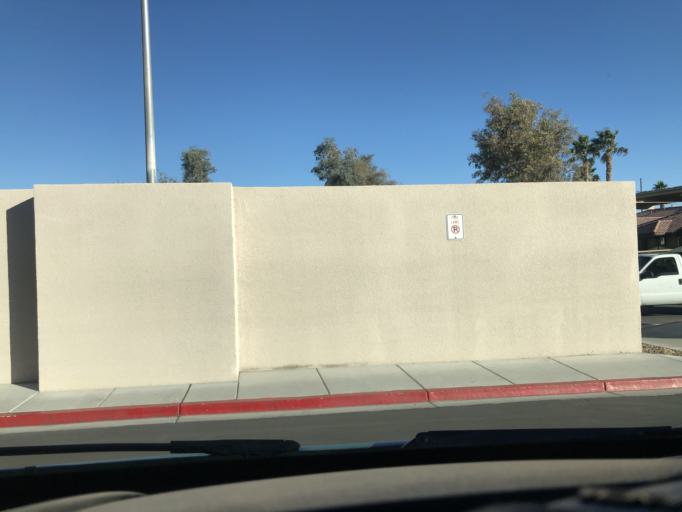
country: US
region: Nevada
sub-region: Clark County
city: North Las Vegas
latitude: 36.1757
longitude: -115.1132
